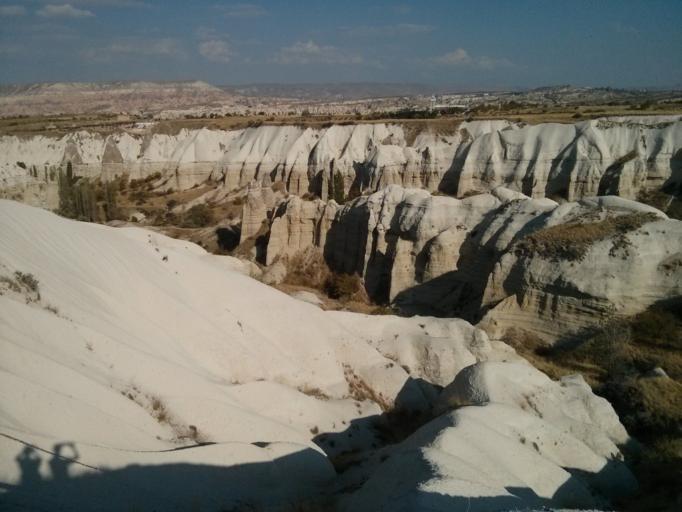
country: TR
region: Nevsehir
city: Goereme
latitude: 38.6351
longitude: 34.8114
